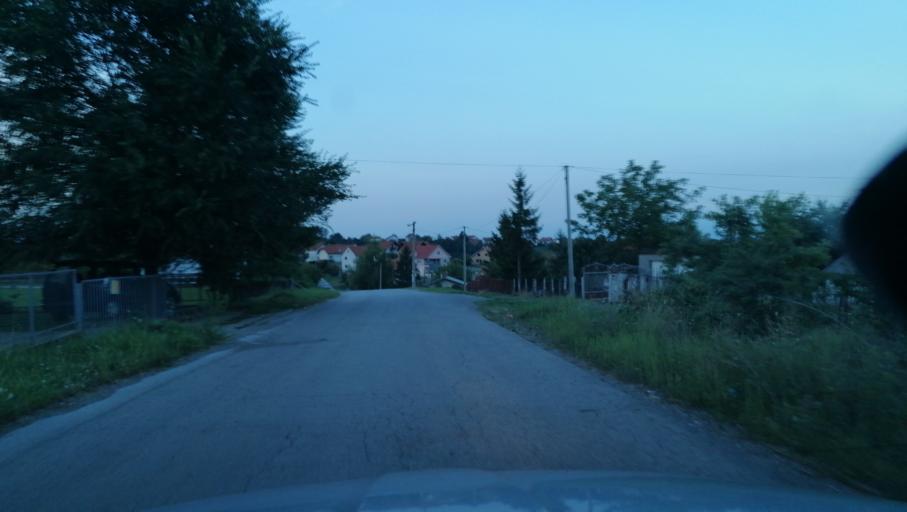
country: RS
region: Central Serbia
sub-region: Kolubarski Okrug
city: Valjevo
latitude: 44.2547
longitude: 19.8760
